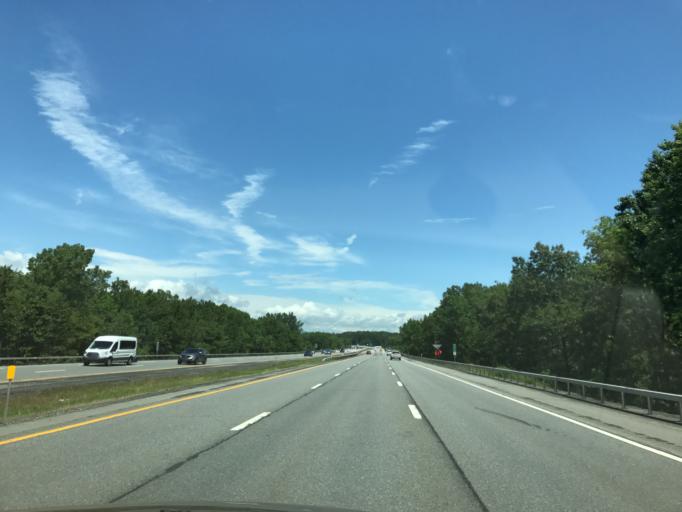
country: US
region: New York
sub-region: Warren County
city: West Glens Falls
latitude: 43.2593
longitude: -73.6786
